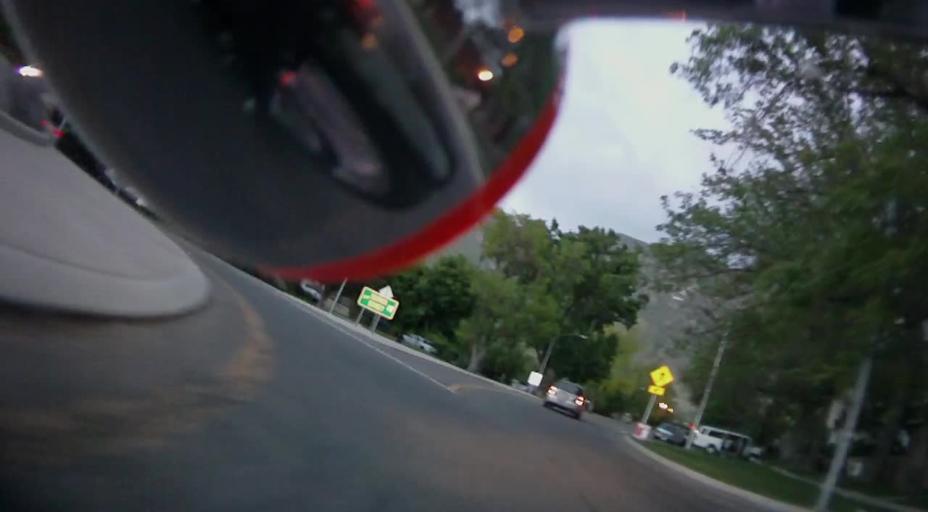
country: US
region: Utah
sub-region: Utah County
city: Provo
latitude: 40.2336
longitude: -111.6465
